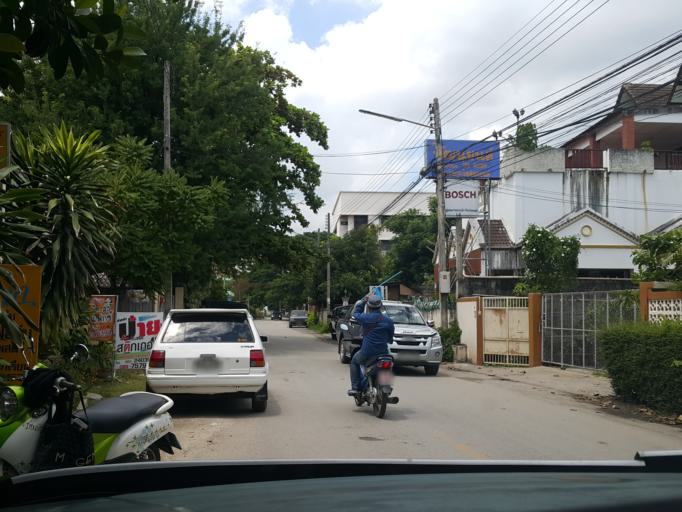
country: TH
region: Chiang Mai
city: Chiang Mai
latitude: 18.7890
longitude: 99.0110
